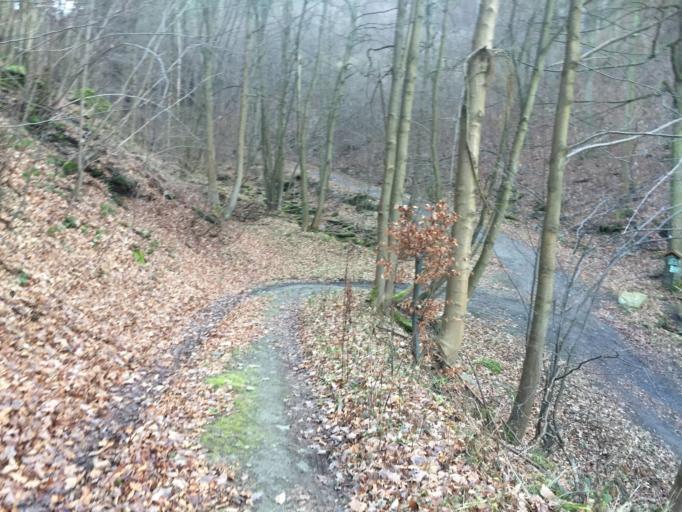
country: DE
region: Thuringia
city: Bad Blankenburg
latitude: 50.6616
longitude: 11.2631
